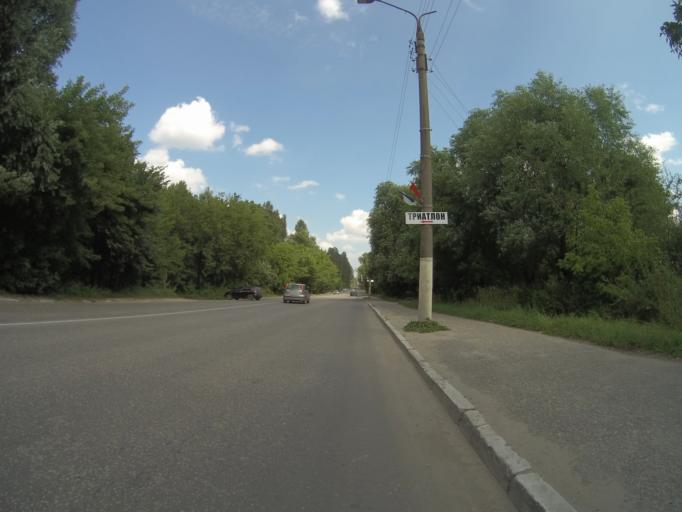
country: RU
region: Vladimir
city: Gus'-Khrustal'nyy
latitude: 55.6276
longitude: 40.6875
